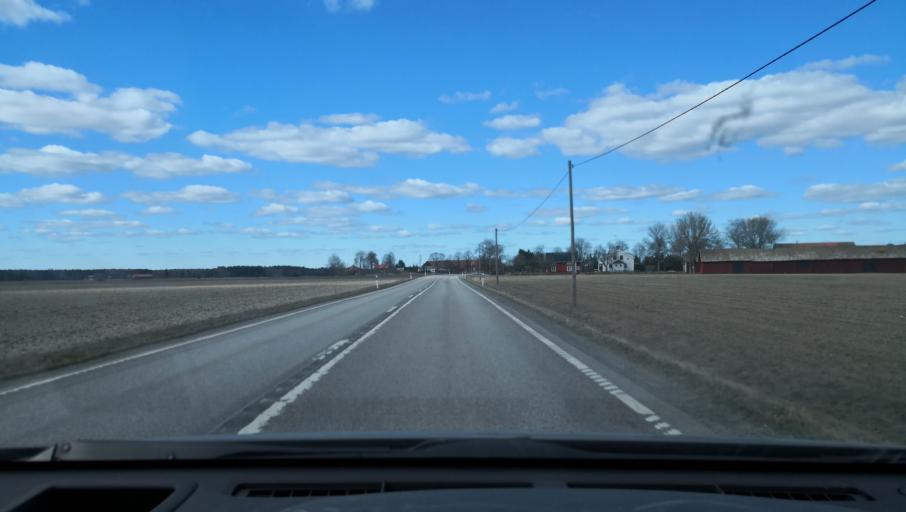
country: SE
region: Vaestmanland
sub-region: Sala Kommun
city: Sala
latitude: 59.8610
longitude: 16.6328
